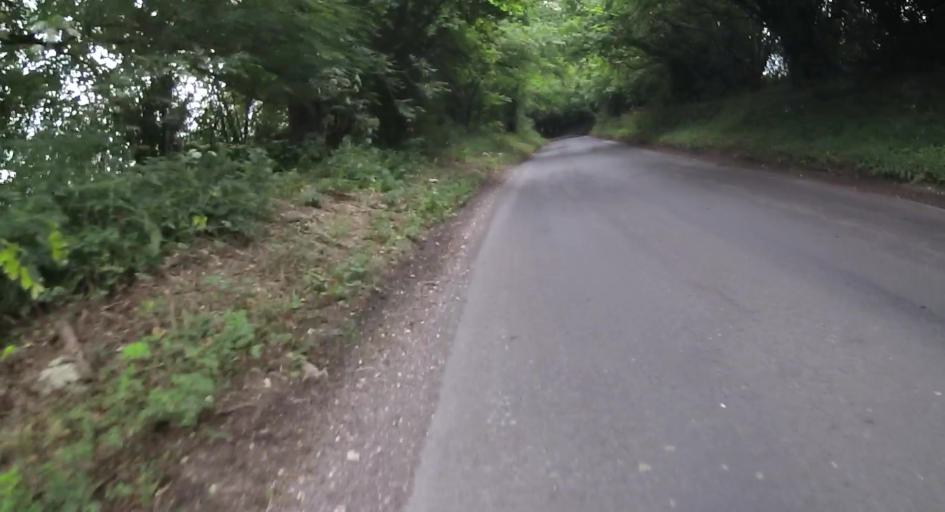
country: GB
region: England
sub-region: Hampshire
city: Bishops Waltham
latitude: 51.0247
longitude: -1.2026
